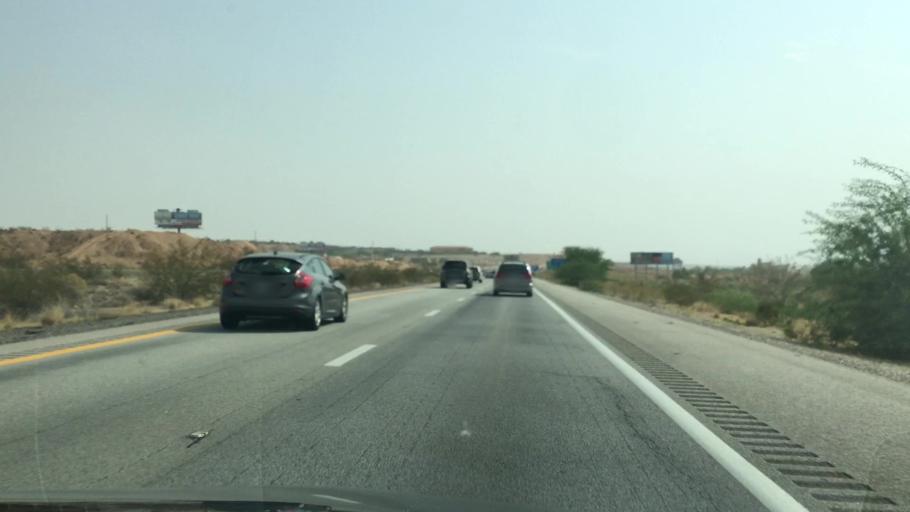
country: US
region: Nevada
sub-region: Clark County
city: Bunkerville
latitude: 36.7956
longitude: -114.1187
